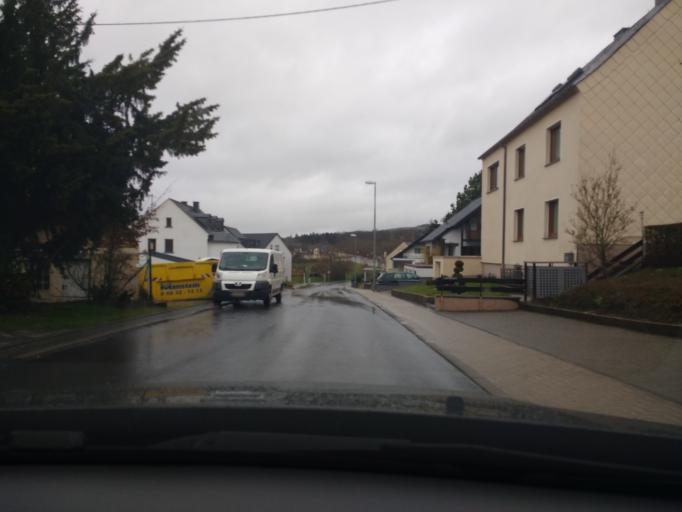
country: DE
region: Rheinland-Pfalz
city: Irsch
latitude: 49.7254
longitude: 6.7027
